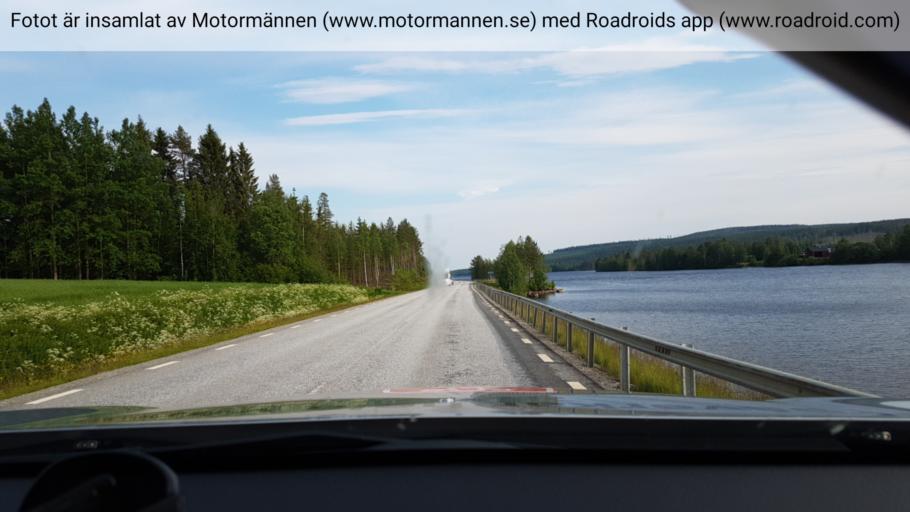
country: SE
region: Vaesterbotten
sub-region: Vindelns Kommun
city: Vindeln
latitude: 64.1810
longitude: 19.4768
